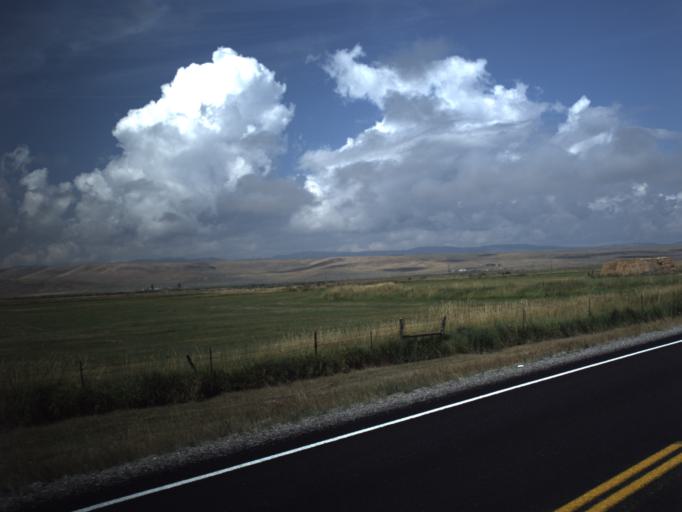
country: US
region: Utah
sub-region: Rich County
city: Randolph
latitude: 41.6399
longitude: -111.1821
